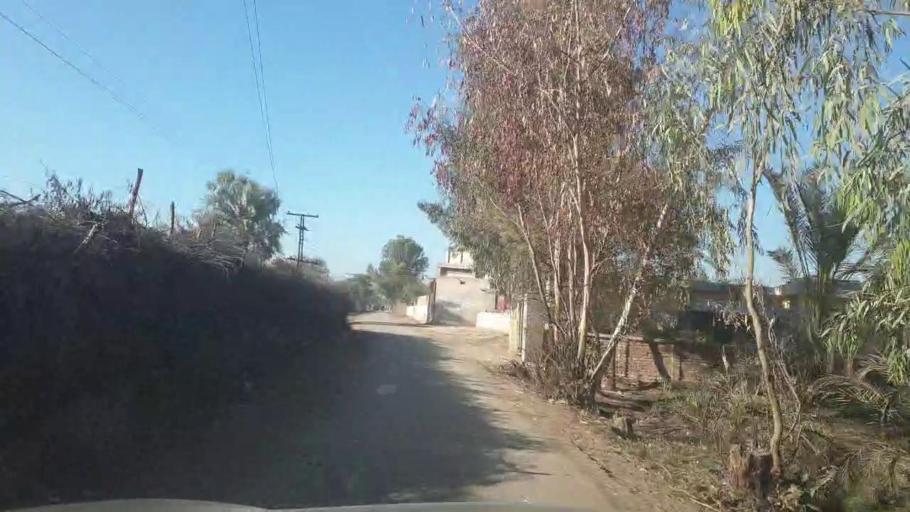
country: PK
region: Sindh
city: Adilpur
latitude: 27.9300
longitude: 69.2559
